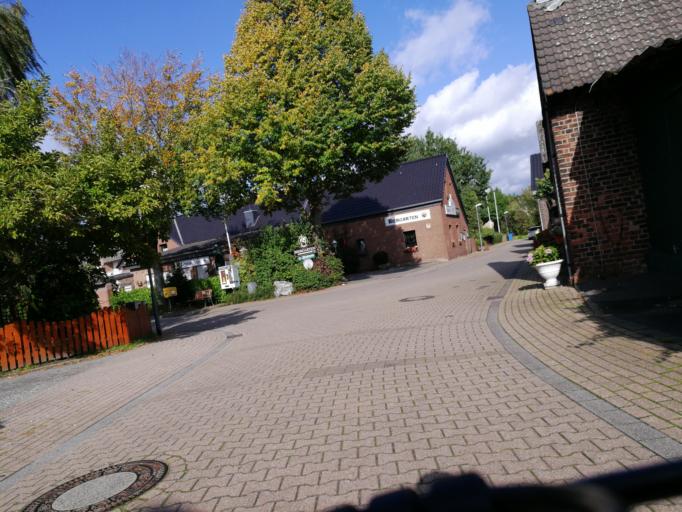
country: DE
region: North Rhine-Westphalia
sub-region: Regierungsbezirk Dusseldorf
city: Dusseldorf
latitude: 51.1478
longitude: 6.7505
